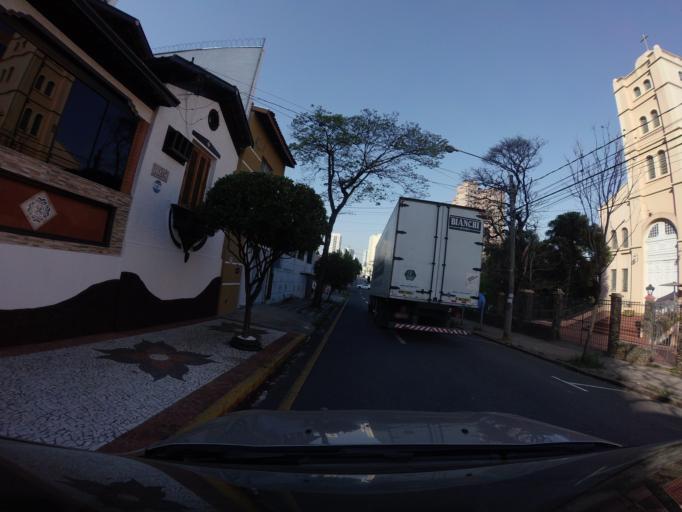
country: BR
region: Sao Paulo
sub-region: Piracicaba
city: Piracicaba
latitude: -22.7254
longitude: -47.6520
